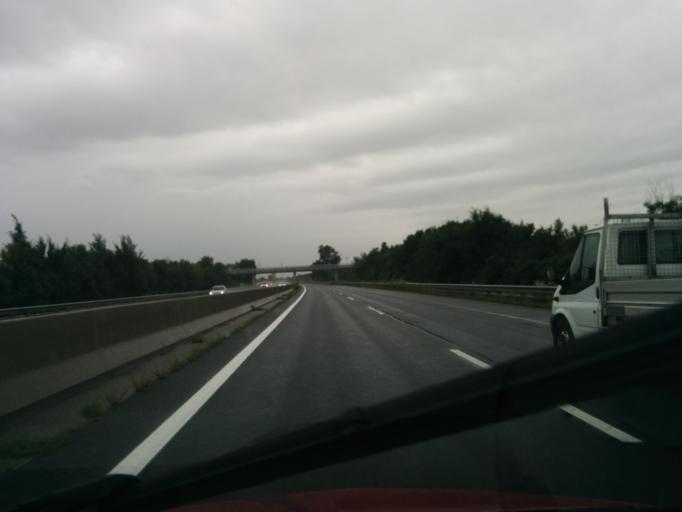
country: AT
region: Lower Austria
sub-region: Politischer Bezirk Baden
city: Trumau
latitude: 47.9735
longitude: 16.3697
